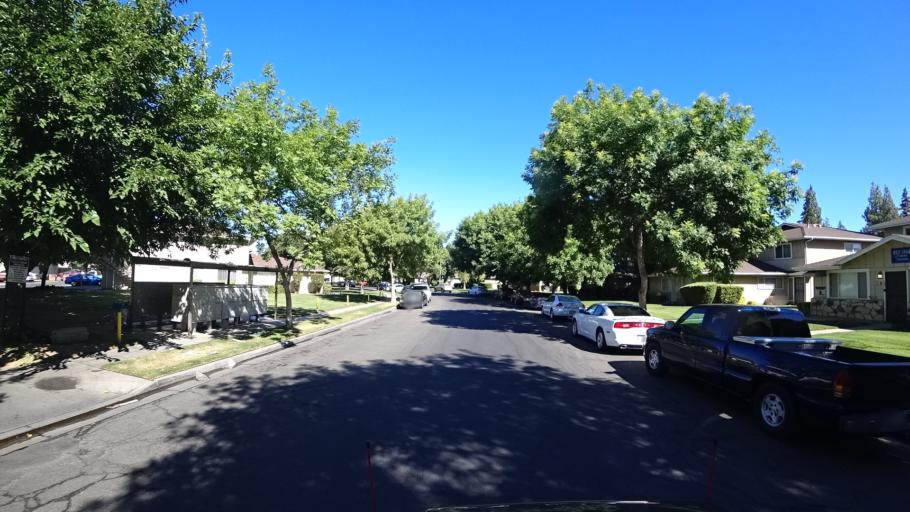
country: US
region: California
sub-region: Fresno County
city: Fresno
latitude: 36.8072
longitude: -119.8409
